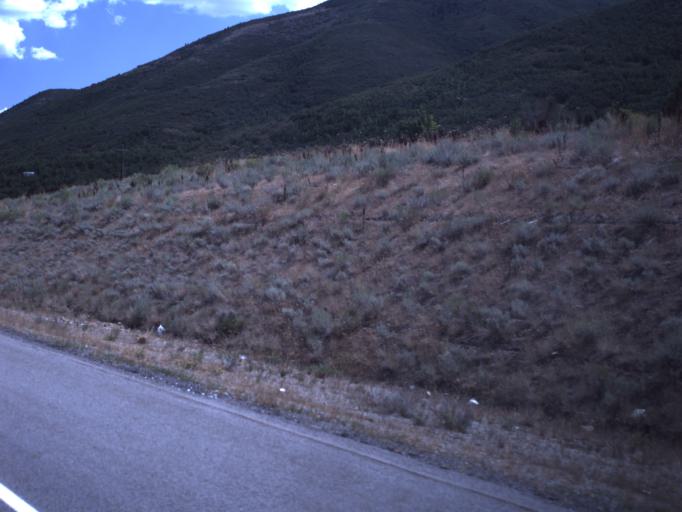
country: US
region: Utah
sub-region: Wasatch County
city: Midway
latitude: 40.4096
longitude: -111.5045
